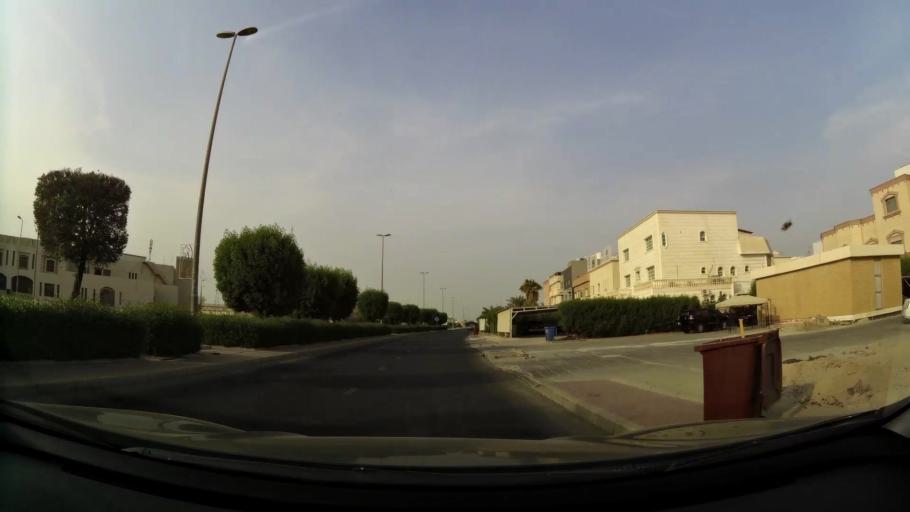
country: KW
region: Mubarak al Kabir
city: Mubarak al Kabir
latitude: 29.1868
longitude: 48.0803
